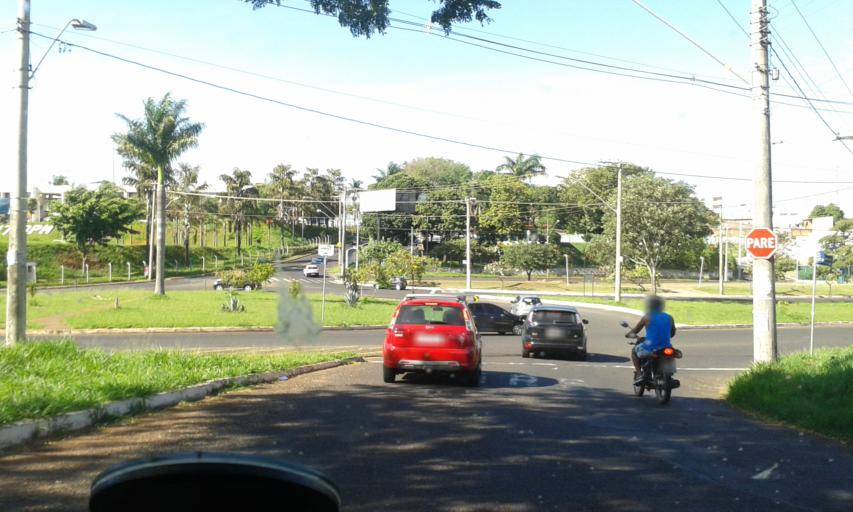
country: BR
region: Minas Gerais
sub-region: Uberlandia
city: Uberlandia
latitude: -18.9091
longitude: -48.2461
